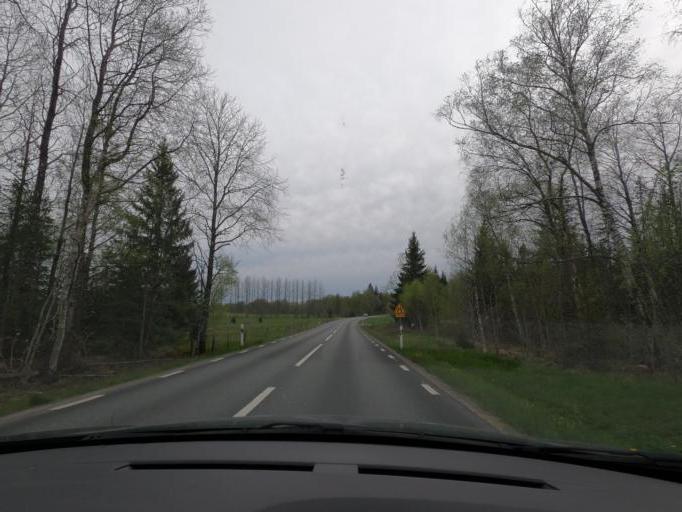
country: SE
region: Joenkoeping
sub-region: Varnamo Kommun
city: Bredaryd
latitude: 57.1876
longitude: 13.7573
